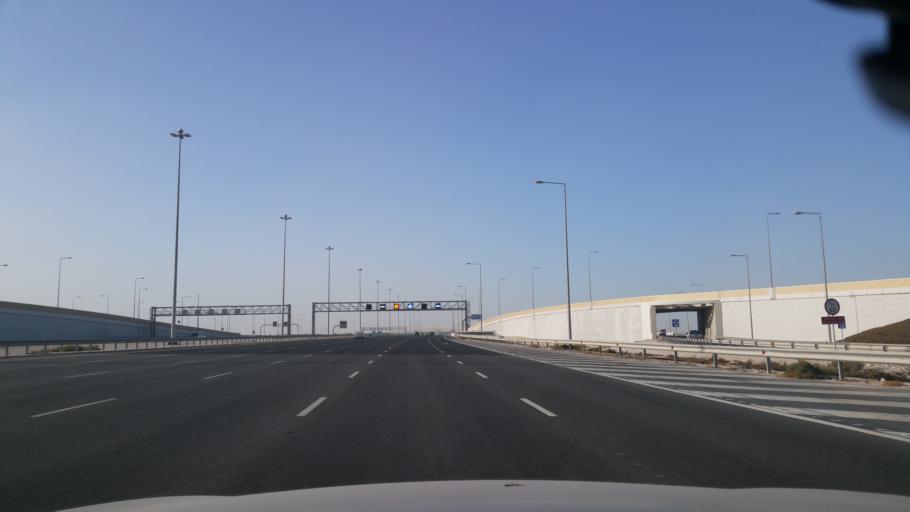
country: QA
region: Al Wakrah
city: Al Wukayr
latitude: 25.1865
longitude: 51.5472
